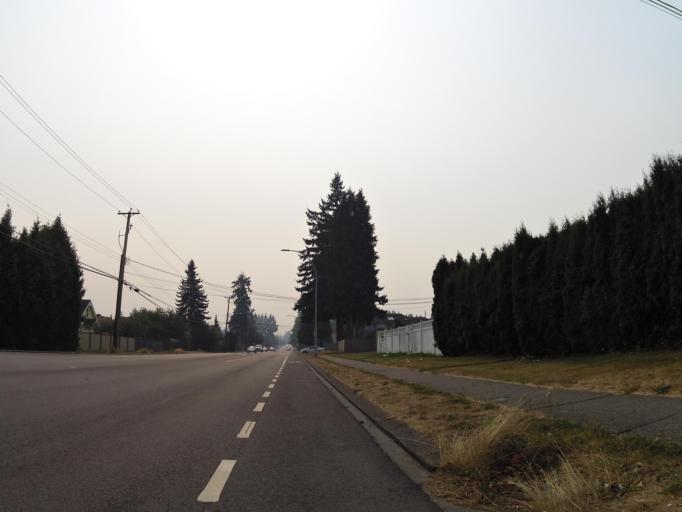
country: CA
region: British Columbia
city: Surrey
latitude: 49.1241
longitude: -122.8566
